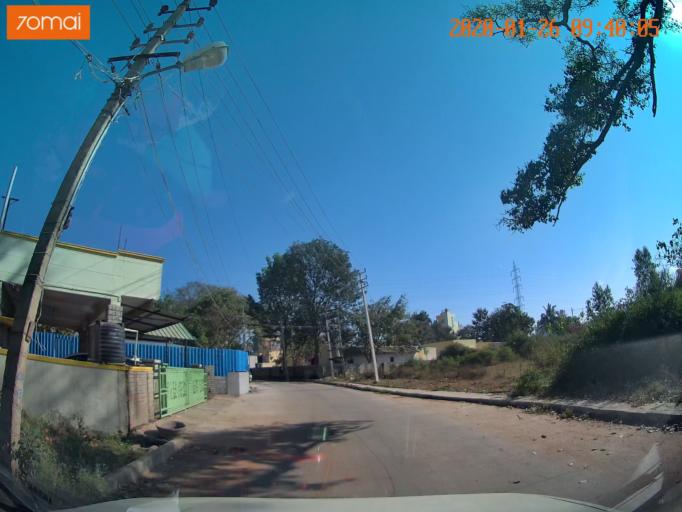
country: IN
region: Karnataka
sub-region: Bangalore Urban
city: Anekal
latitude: 12.8320
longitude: 77.6385
